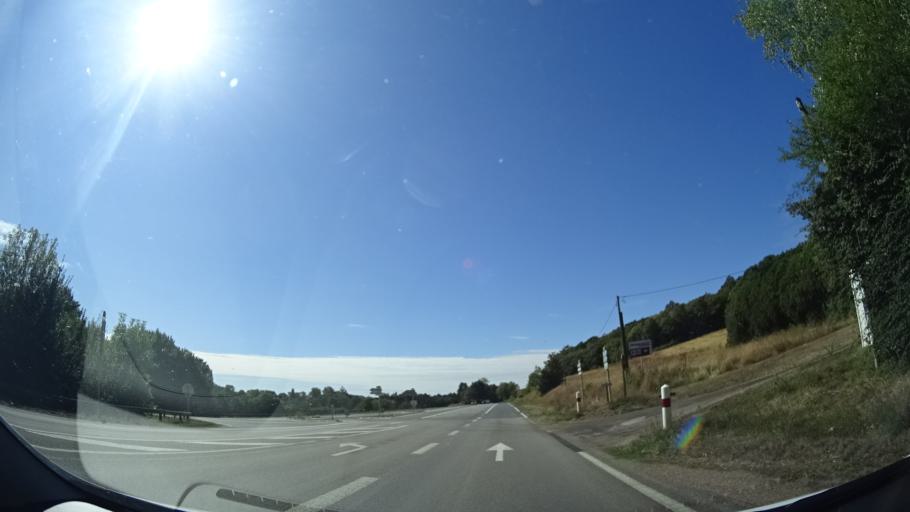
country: FR
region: Centre
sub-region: Departement du Loiret
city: Douchy
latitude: 47.9360
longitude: 3.0800
